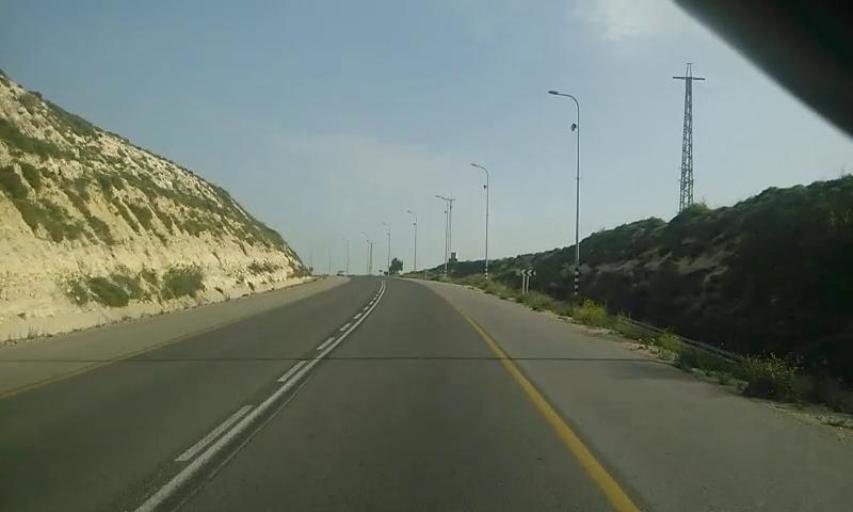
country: PS
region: West Bank
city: Sarrah
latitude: 32.1969
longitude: 35.1858
